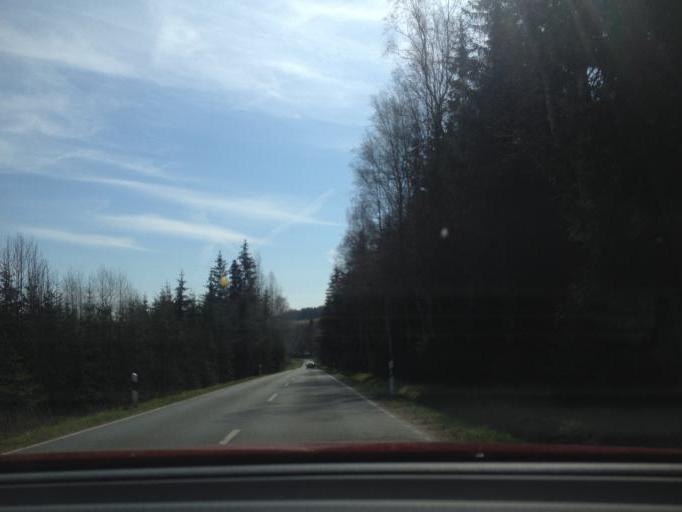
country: DE
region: Bavaria
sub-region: Upper Franconia
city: Grub
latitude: 50.0902
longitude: 11.9129
